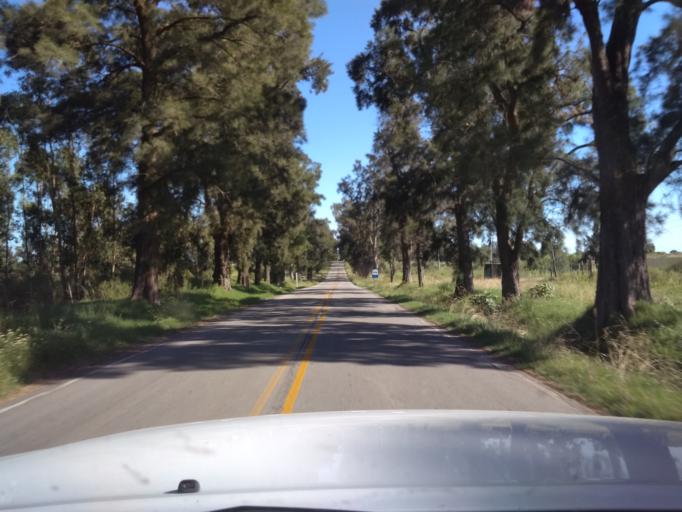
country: UY
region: Canelones
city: San Bautista
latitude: -34.3706
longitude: -55.9595
